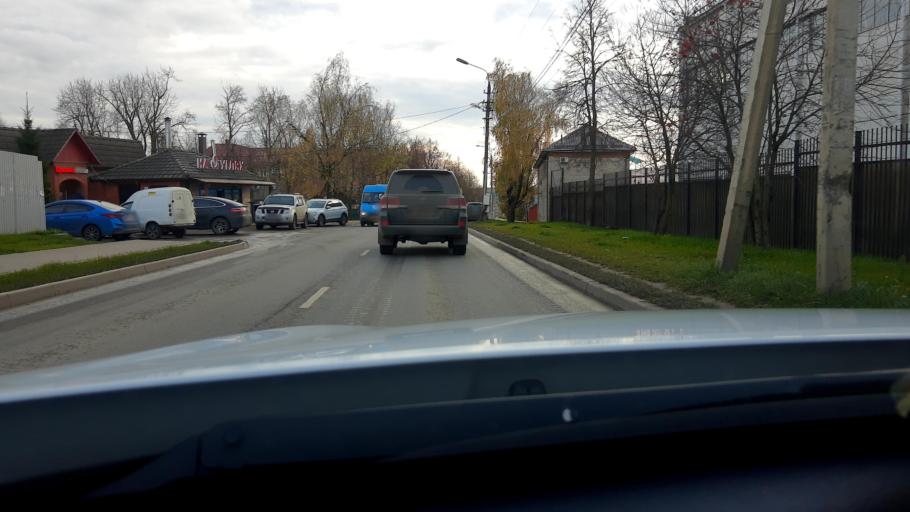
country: RU
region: Moskovskaya
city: Kokoshkino
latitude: 55.5390
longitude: 37.1539
